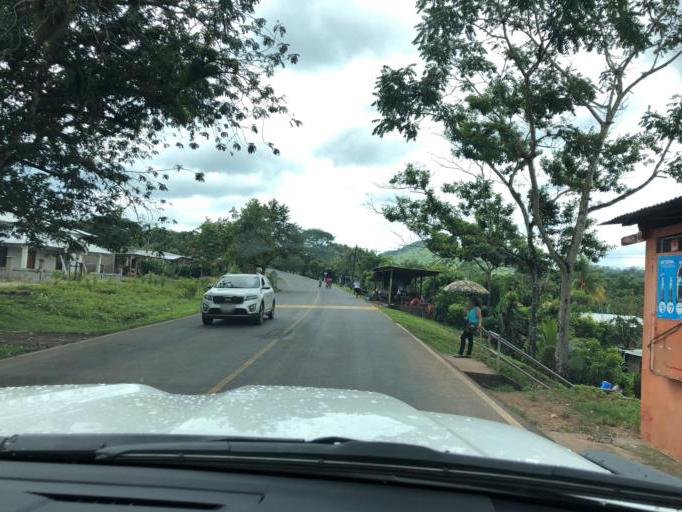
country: NI
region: Chontales
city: Villa Sandino
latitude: 11.9922
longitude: -84.8655
